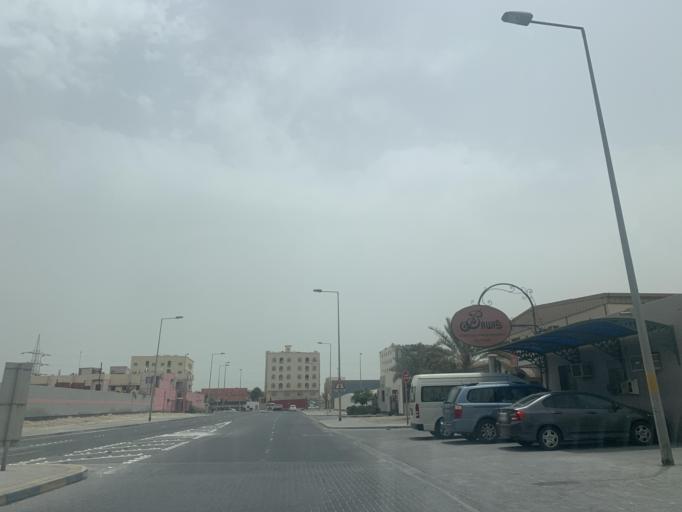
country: BH
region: Northern
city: Sitrah
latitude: 26.1773
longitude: 50.6035
